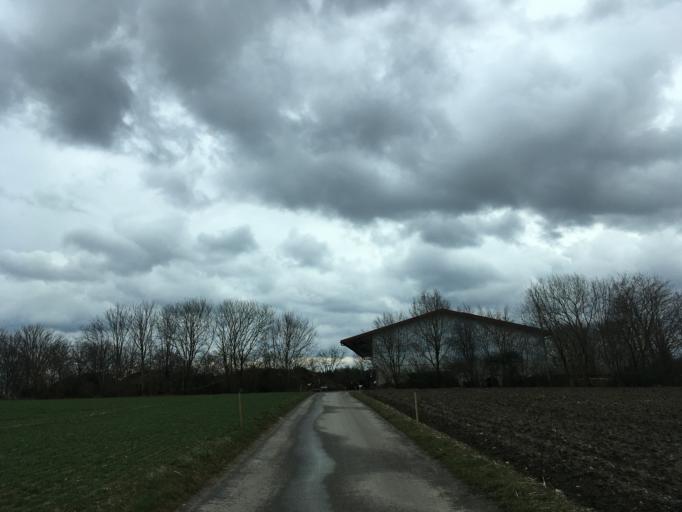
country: DE
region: Bavaria
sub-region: Upper Bavaria
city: Markt Schwaben
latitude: 48.1750
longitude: 11.8604
